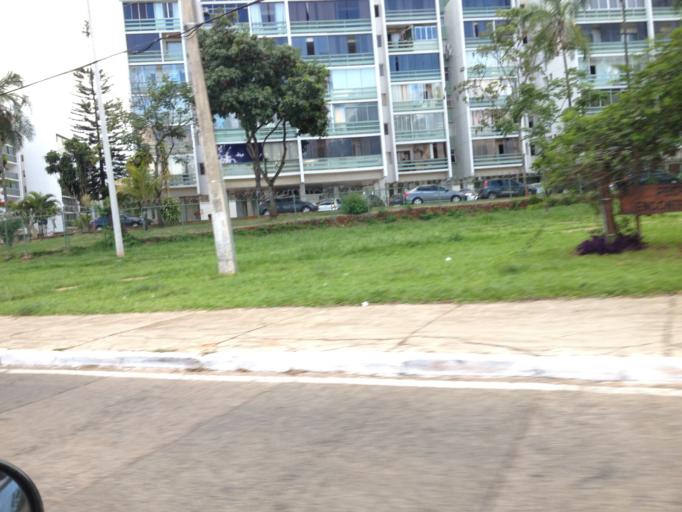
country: BR
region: Federal District
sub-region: Brasilia
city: Brasilia
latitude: -15.8091
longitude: -47.9405
